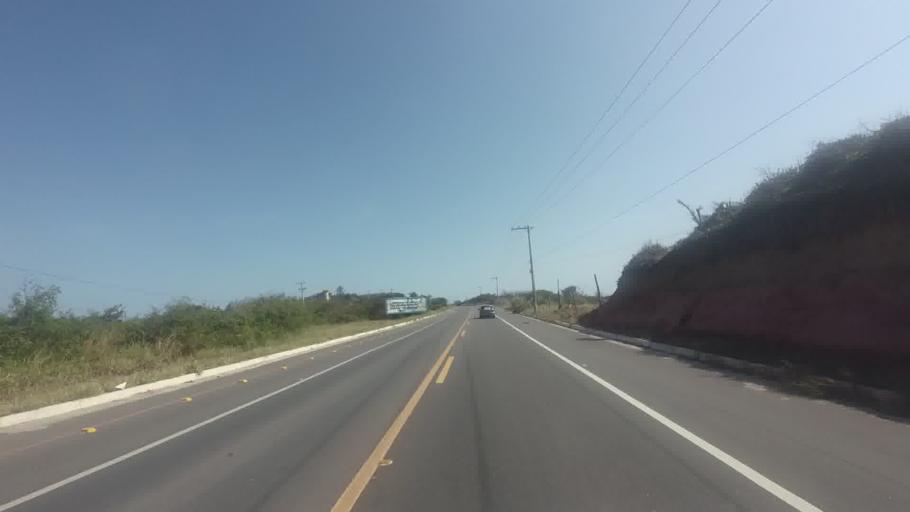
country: BR
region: Espirito Santo
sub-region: Piuma
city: Piuma
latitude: -20.8159
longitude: -40.6145
